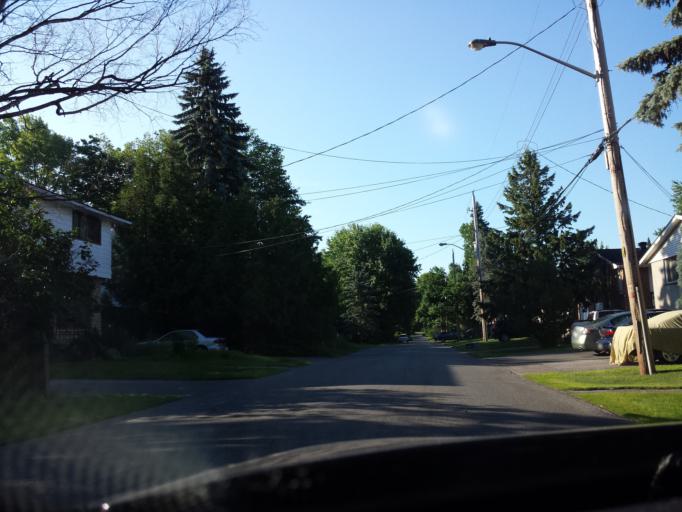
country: CA
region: Ontario
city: Bells Corners
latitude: 45.3701
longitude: -75.8006
